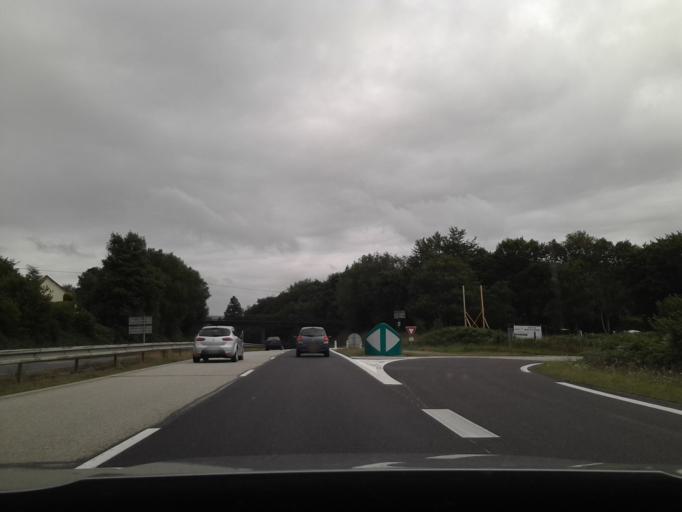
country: FR
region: Lower Normandy
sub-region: Departement de la Manche
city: Brix
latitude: 49.5508
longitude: -1.5611
